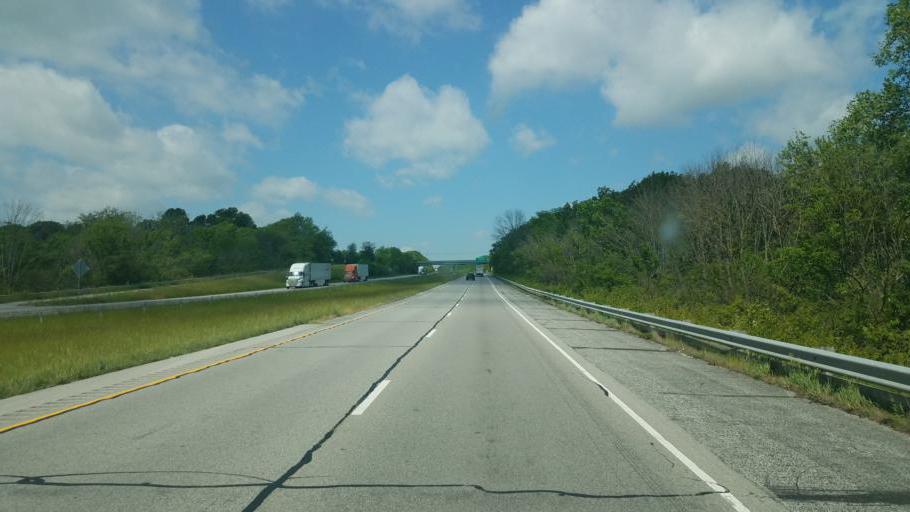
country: US
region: Indiana
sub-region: Vigo County
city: West Terre Haute
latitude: 39.4487
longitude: -87.4650
